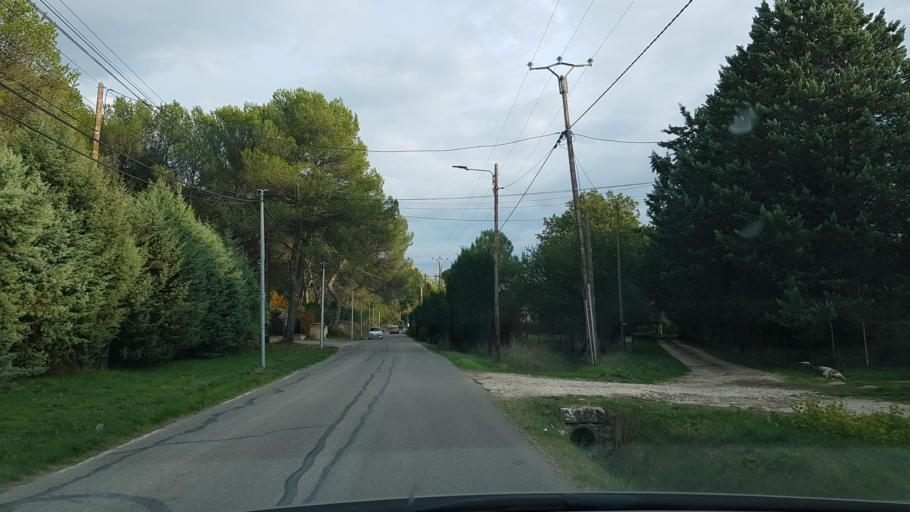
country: FR
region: Provence-Alpes-Cote d'Azur
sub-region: Departement des Bouches-du-Rhone
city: Cabries
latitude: 43.4495
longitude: 5.3642
